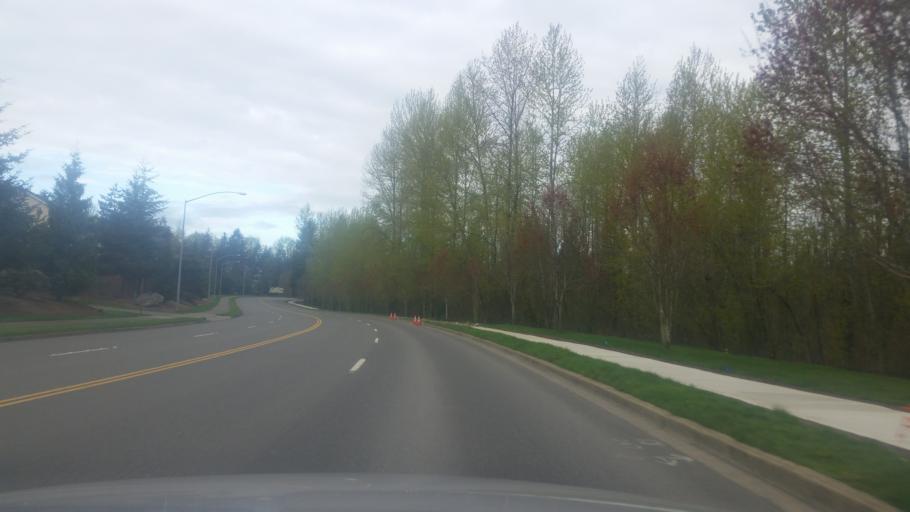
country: US
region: Washington
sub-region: Pierce County
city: South Hill
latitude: 47.1124
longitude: -122.2548
